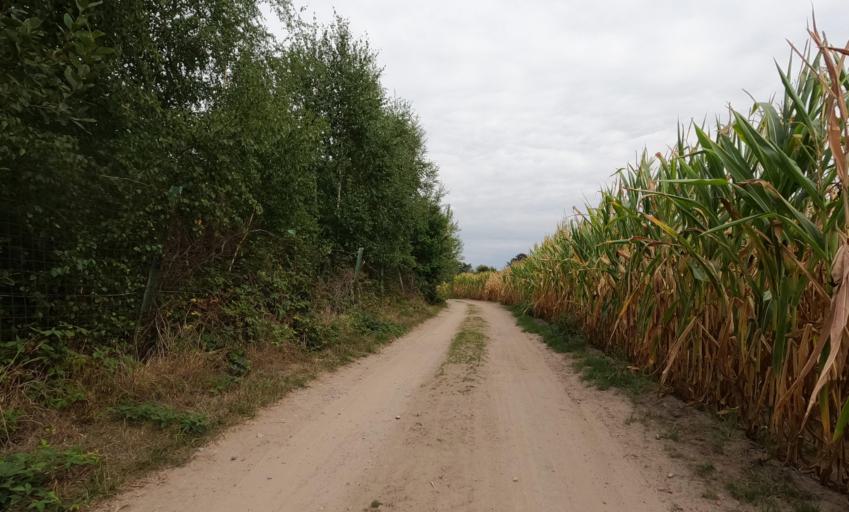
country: BE
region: Flanders
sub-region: Provincie Oost-Vlaanderen
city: Buggenhout
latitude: 51.0331
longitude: 4.2088
